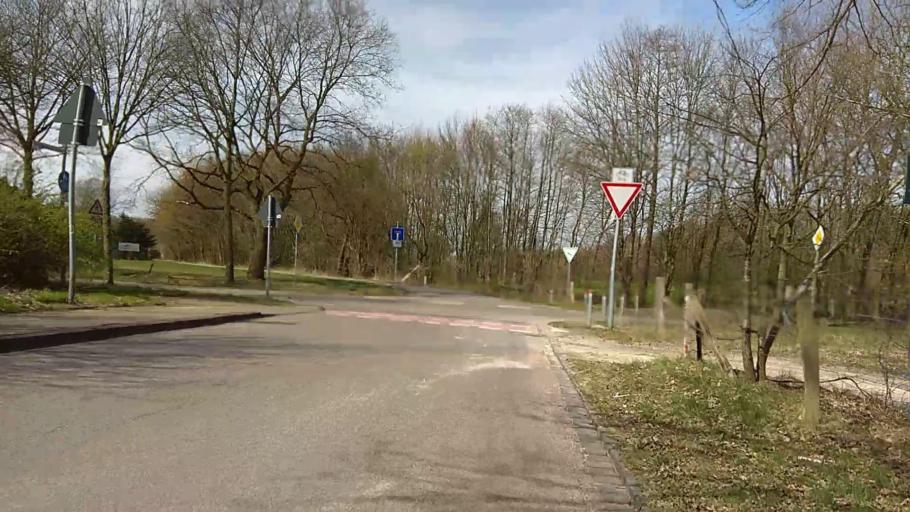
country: DE
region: North Rhine-Westphalia
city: Herten
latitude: 51.5664
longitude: 7.1038
